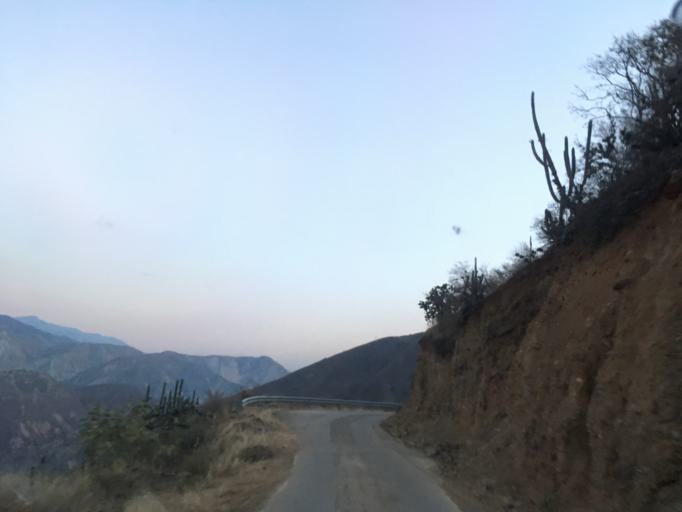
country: CO
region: Santander
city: Aratoca
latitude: 6.7815
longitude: -72.9936
